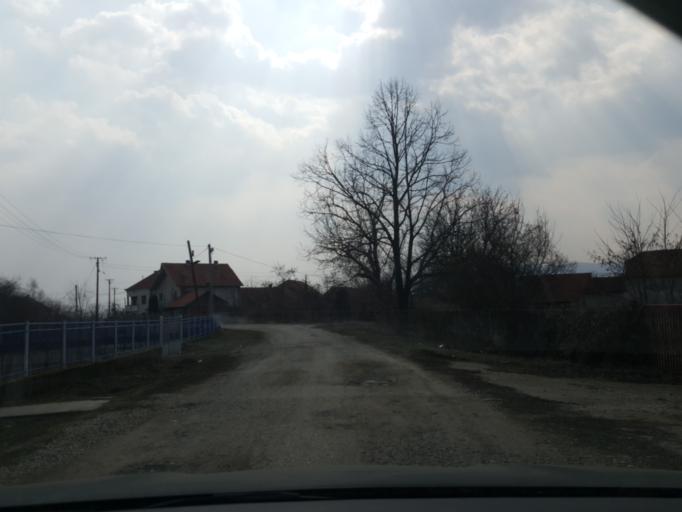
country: RS
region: Central Serbia
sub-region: Nisavski Okrug
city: Aleksinac
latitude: 43.4489
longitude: 21.7912
